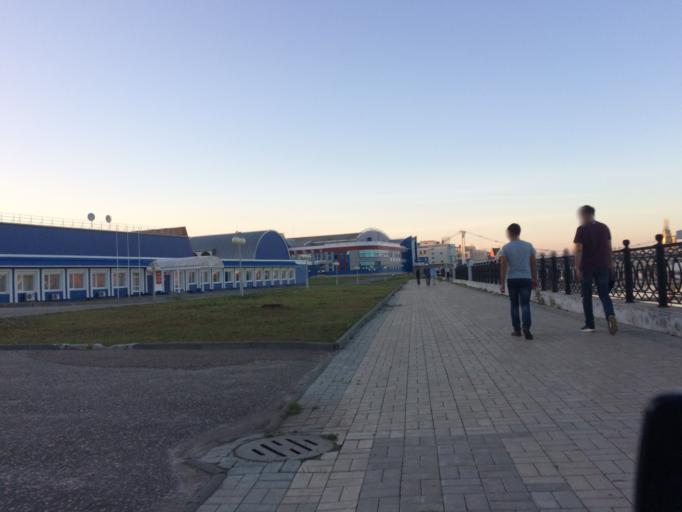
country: RU
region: Mariy-El
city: Yoshkar-Ola
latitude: 56.6245
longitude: 47.8963
